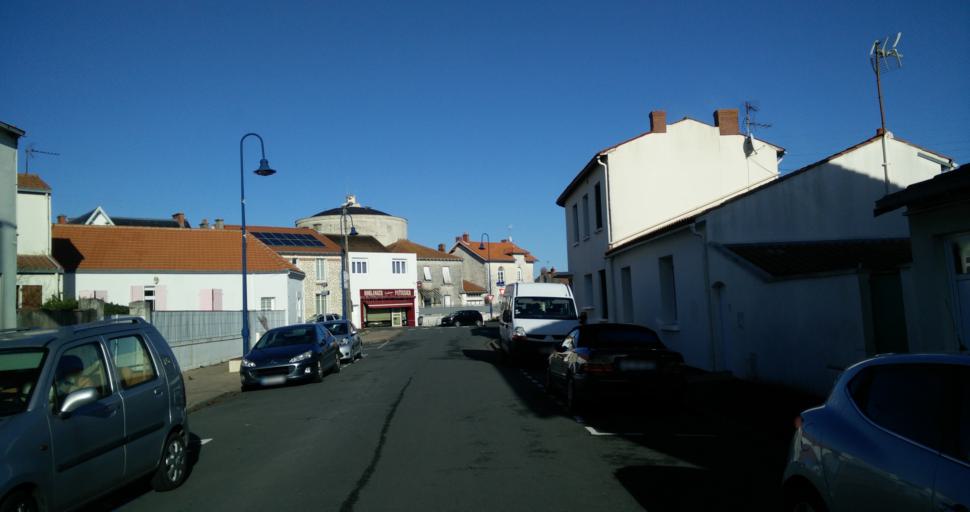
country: FR
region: Poitou-Charentes
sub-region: Departement de la Charente-Maritime
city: La Rochelle
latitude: 46.1637
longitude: -1.2042
